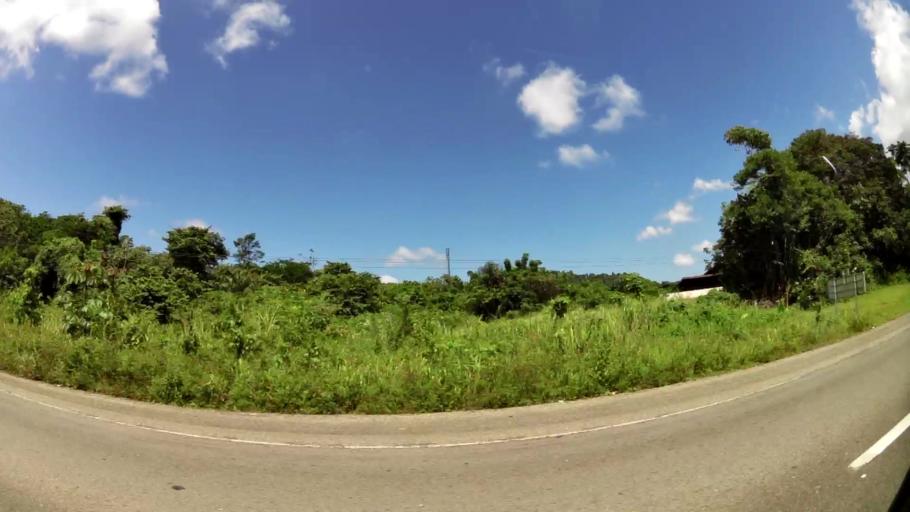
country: GF
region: Guyane
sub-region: Guyane
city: Matoury
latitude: 4.8711
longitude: -52.3369
